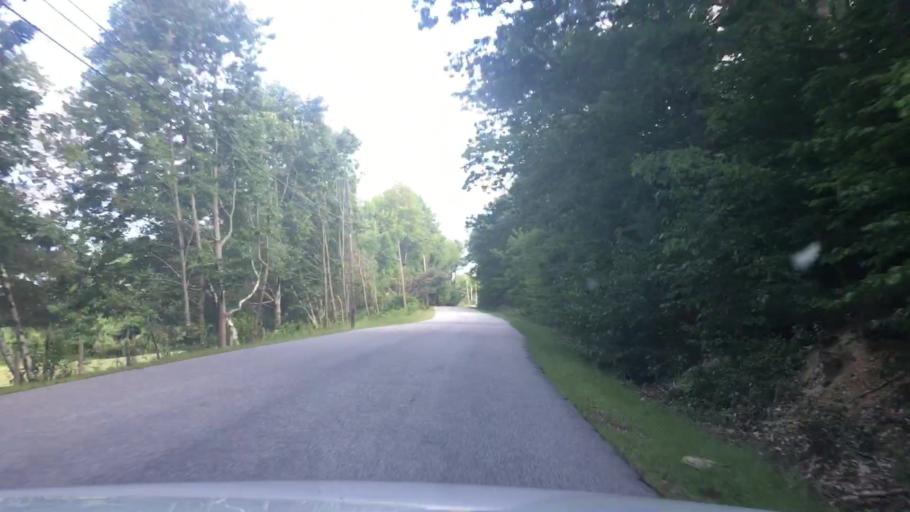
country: US
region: Maine
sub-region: Androscoggin County
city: Auburn
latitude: 44.1672
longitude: -70.2515
